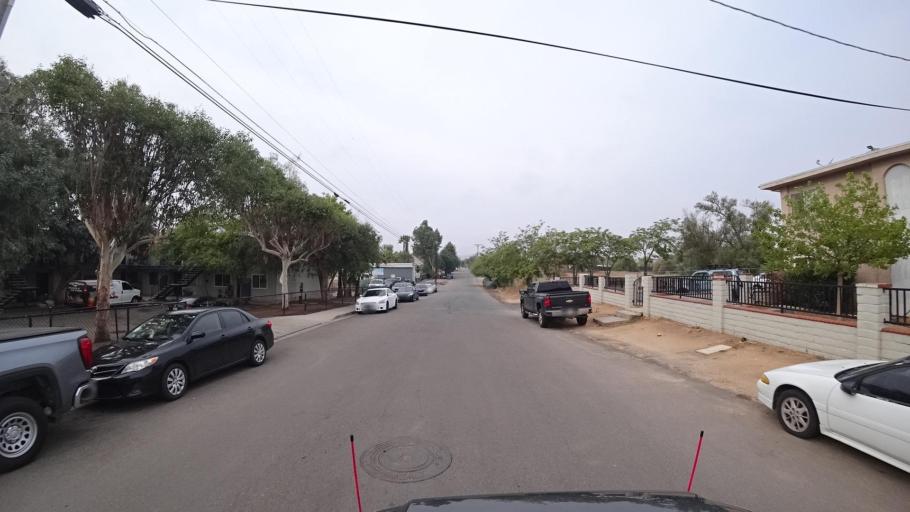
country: US
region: California
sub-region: San Diego County
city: Ramona
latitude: 33.0459
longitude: -116.8661
